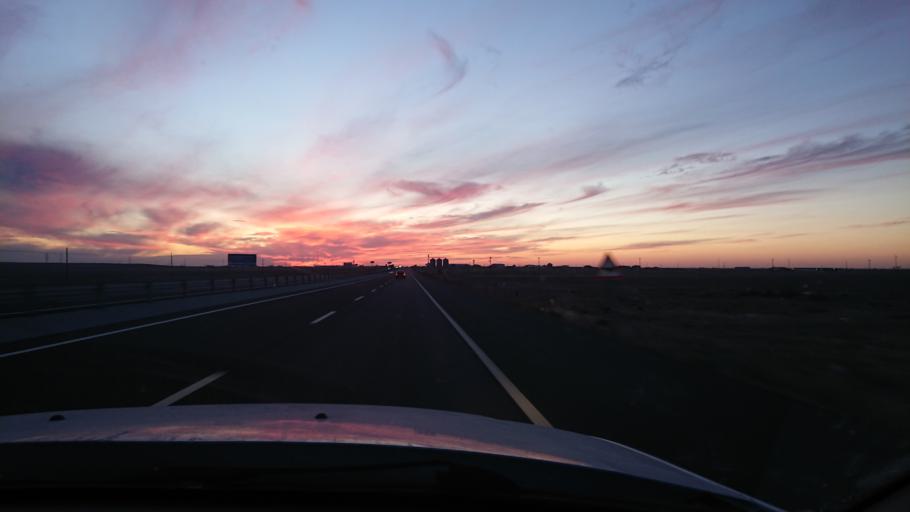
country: TR
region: Aksaray
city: Yesilova
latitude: 38.3309
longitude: 33.9093
